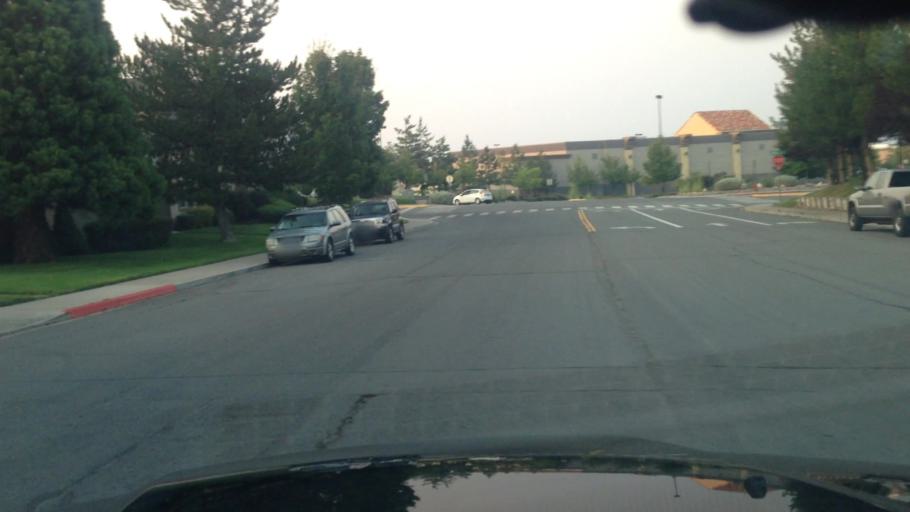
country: US
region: Nevada
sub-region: Washoe County
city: Reno
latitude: 39.4777
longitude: -119.8006
